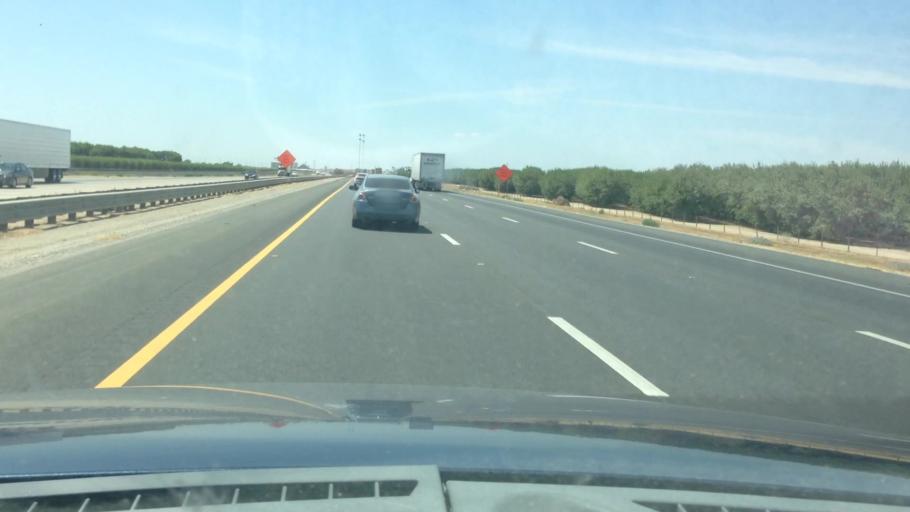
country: US
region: California
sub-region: Kern County
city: McFarland
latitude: 35.6226
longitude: -119.2144
